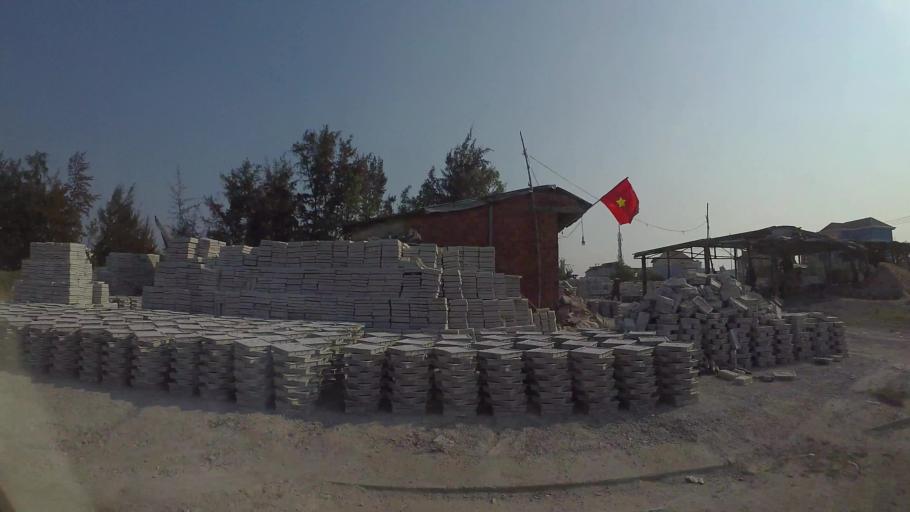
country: VN
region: Da Nang
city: Ngu Hanh Son
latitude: 15.9578
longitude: 108.2562
